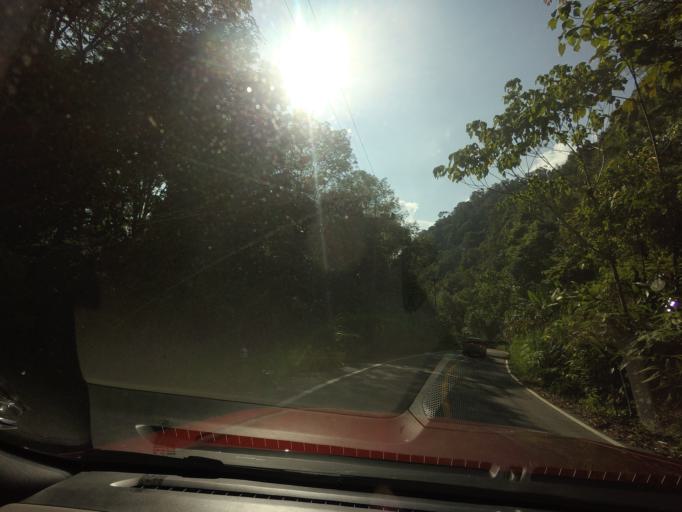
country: TH
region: Yala
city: Than To
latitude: 6.0736
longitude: 101.3447
